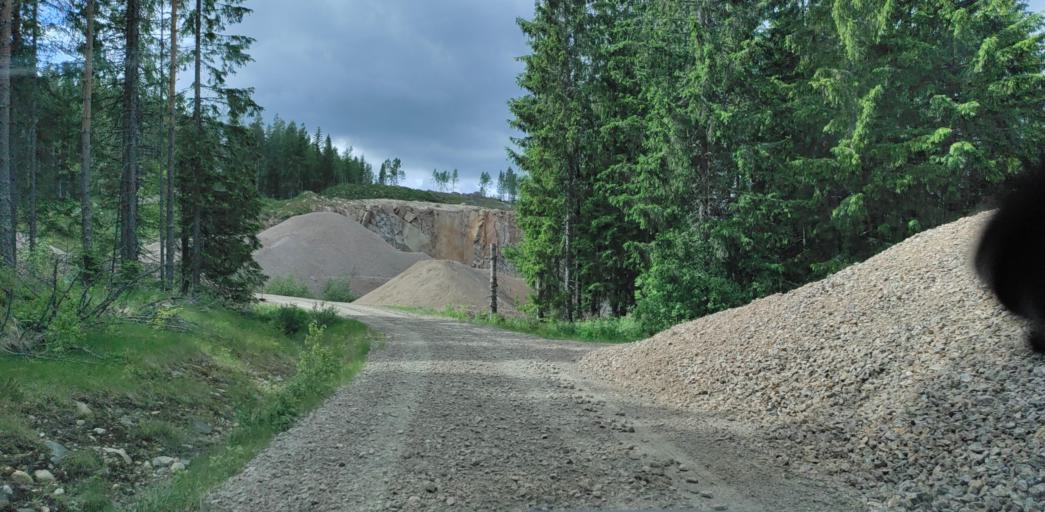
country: SE
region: Vaermland
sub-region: Munkfors Kommun
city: Munkfors
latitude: 59.9542
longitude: 13.4114
